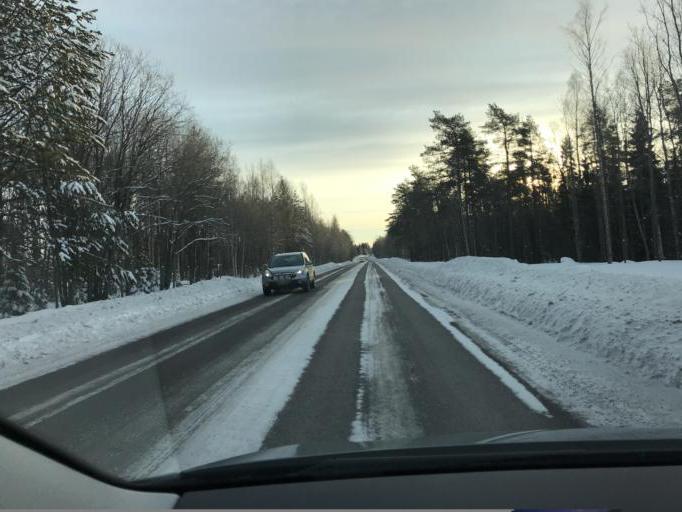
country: SE
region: Norrbotten
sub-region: Lulea Kommun
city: Bergnaset
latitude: 65.6189
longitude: 22.0814
